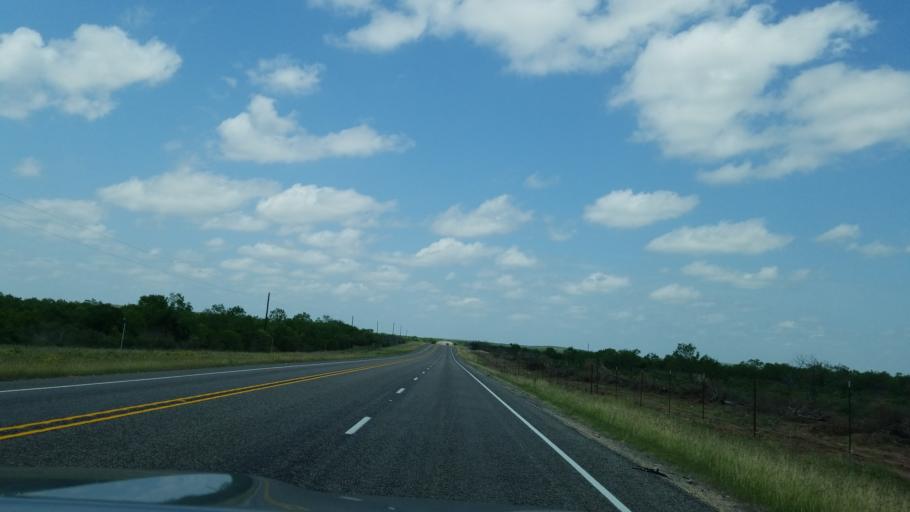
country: US
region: Texas
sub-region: Frio County
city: Pearsall
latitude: 28.9446
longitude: -99.3081
